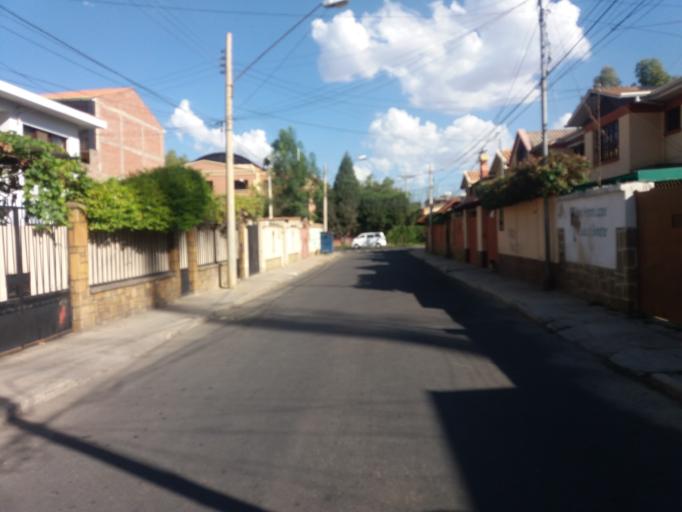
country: BO
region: Cochabamba
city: Cochabamba
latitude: -17.3915
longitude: -66.1445
